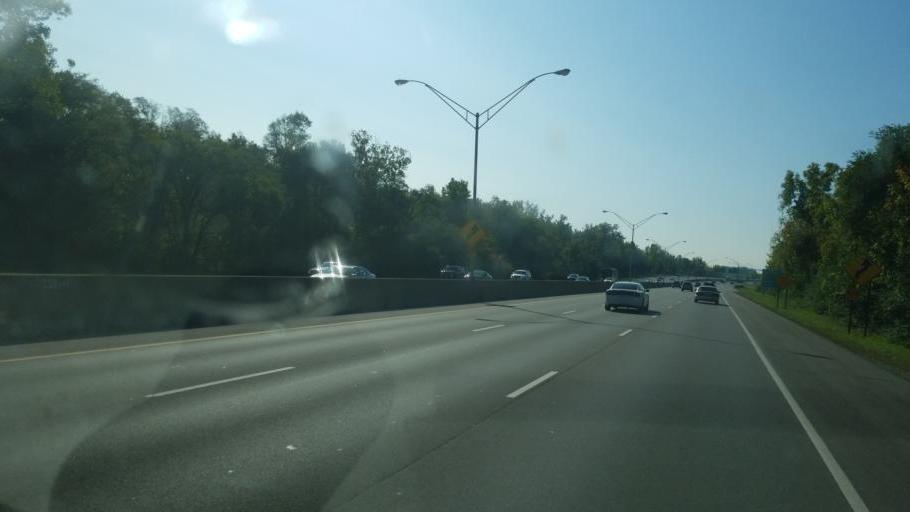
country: US
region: Ohio
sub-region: Franklin County
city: Upper Arlington
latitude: 40.0382
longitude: -83.0303
